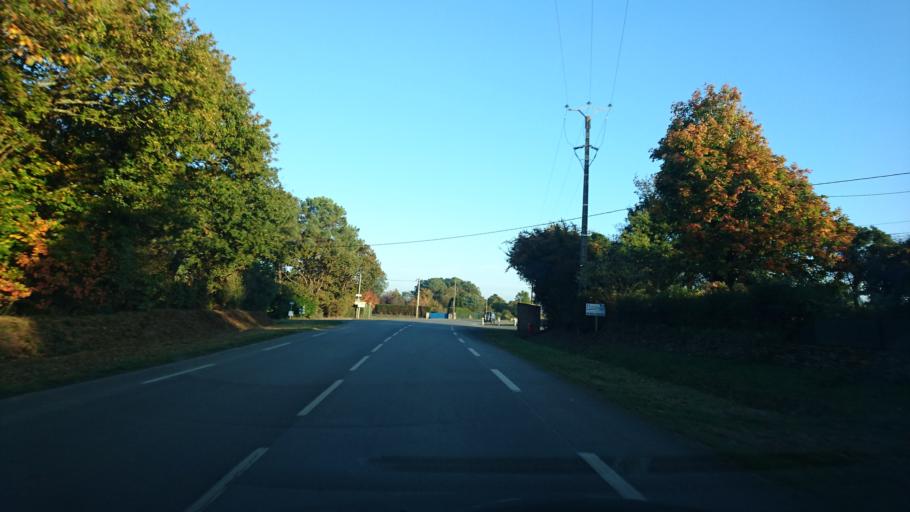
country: FR
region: Brittany
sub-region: Departement du Morbihan
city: Larmor-Baden
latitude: 47.6087
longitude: -2.8788
